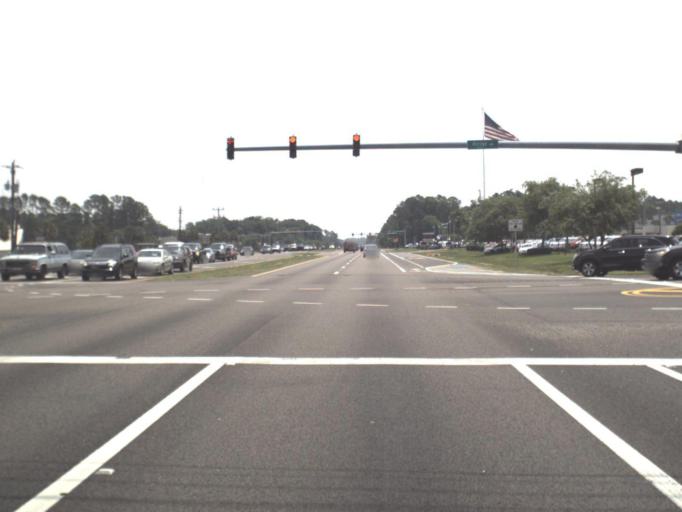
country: US
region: Florida
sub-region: Nassau County
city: Yulee
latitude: 30.6222
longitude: -81.5331
